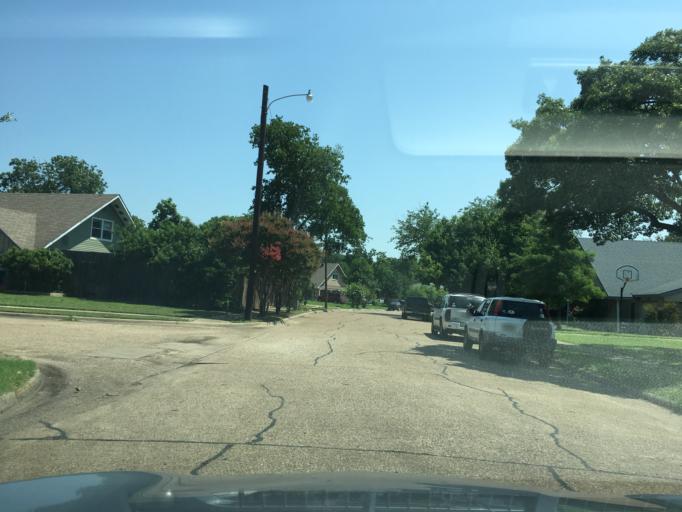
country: US
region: Texas
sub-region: Dallas County
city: Garland
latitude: 32.9192
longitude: -96.6876
